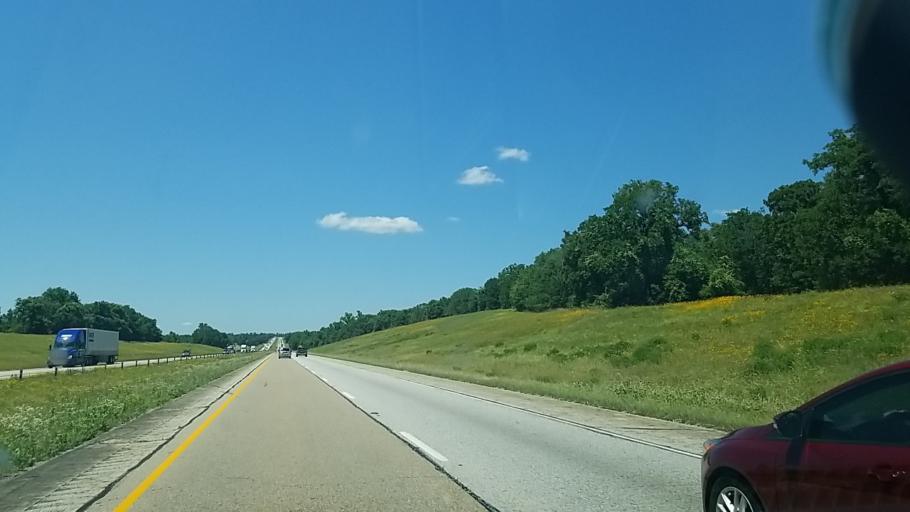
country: US
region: Texas
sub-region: Leon County
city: Centerville
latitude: 31.1783
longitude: -95.9895
